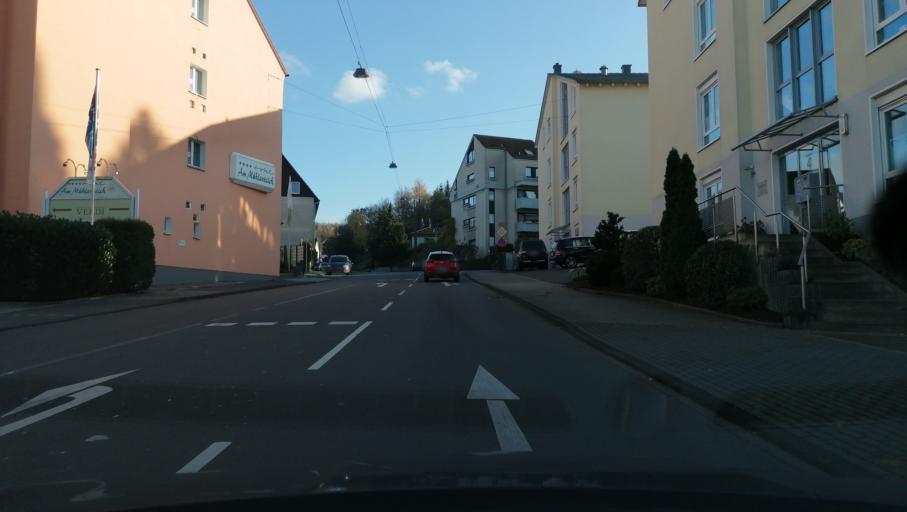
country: DE
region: North Rhine-Westphalia
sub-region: Regierungsbezirk Arnsberg
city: Schwelm
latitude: 51.2828
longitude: 7.2911
